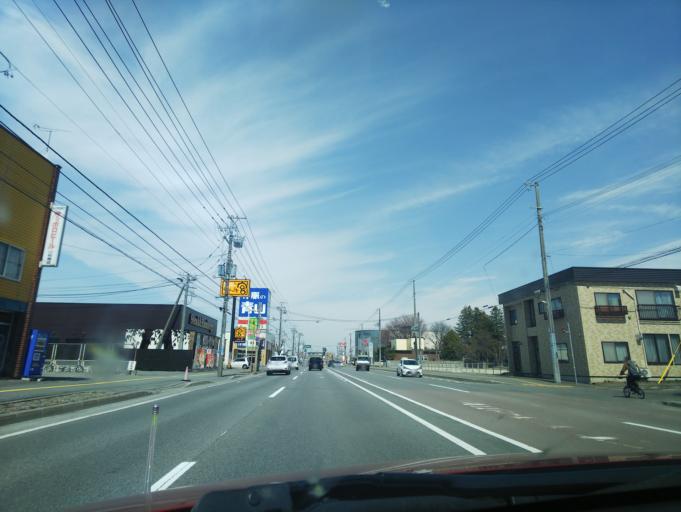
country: JP
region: Hokkaido
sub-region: Asahikawa-shi
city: Asahikawa
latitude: 43.7771
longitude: 142.3848
